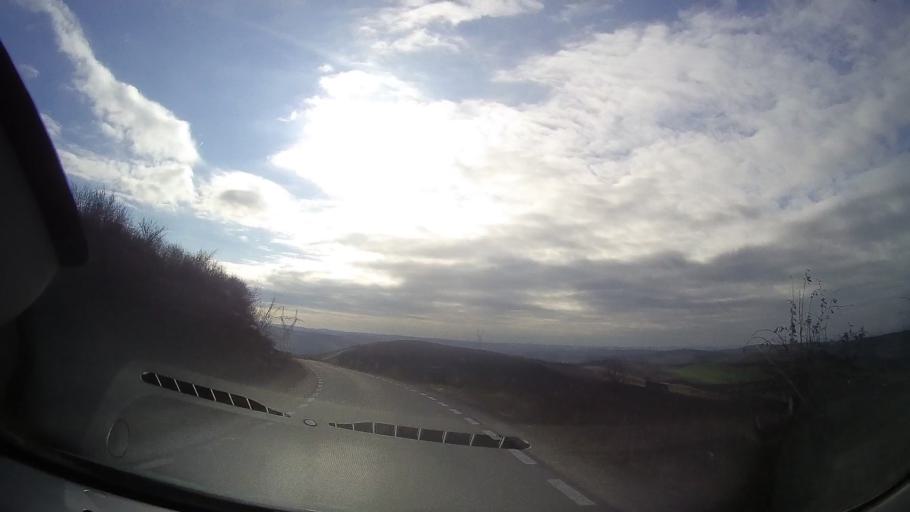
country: RO
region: Mures
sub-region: Comuna Sanger
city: Sanger
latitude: 46.5570
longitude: 24.1601
